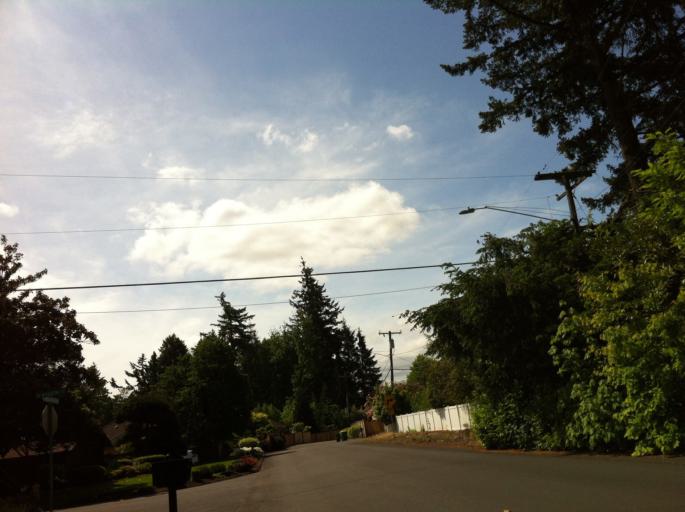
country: US
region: Oregon
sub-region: Washington County
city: West Slope
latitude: 45.4916
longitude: -122.7539
